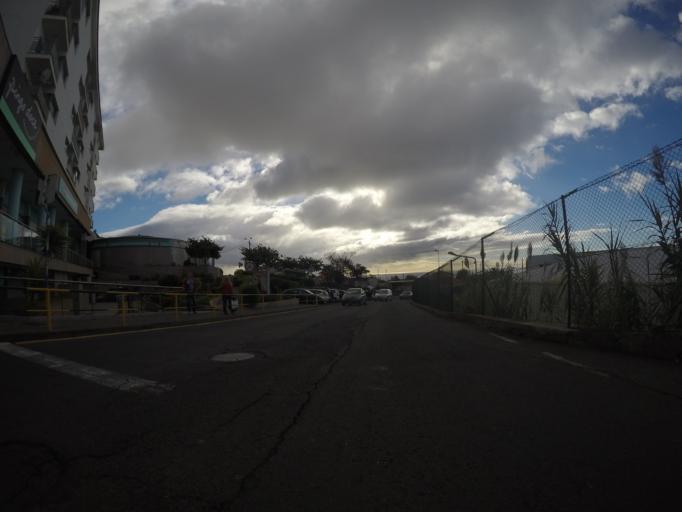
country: PT
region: Madeira
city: Canico
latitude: 32.6464
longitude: -16.8572
